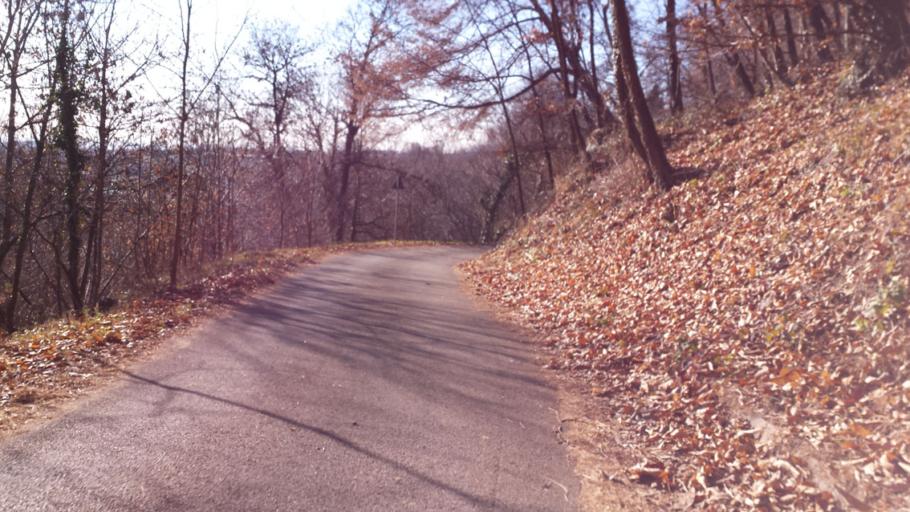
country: IT
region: Veneto
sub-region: Provincia di Treviso
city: Castelcucco
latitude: 45.8371
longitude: 11.8716
